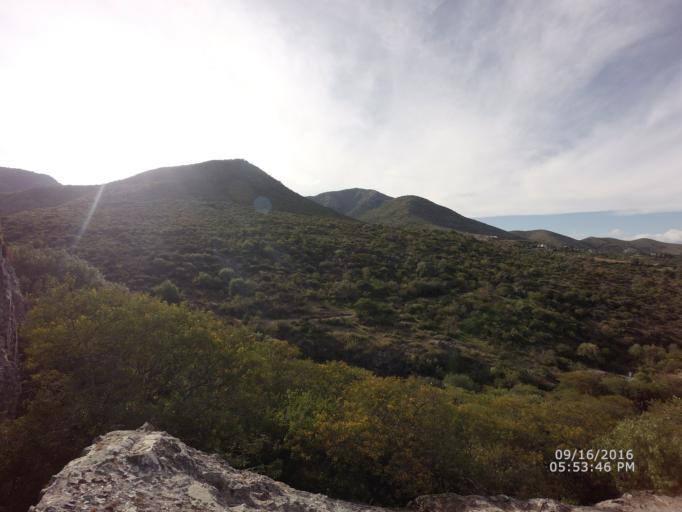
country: MX
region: Queretaro
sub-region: Ezequiel Montes
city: San Jose del Jagueey
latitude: 20.7513
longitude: -99.9499
